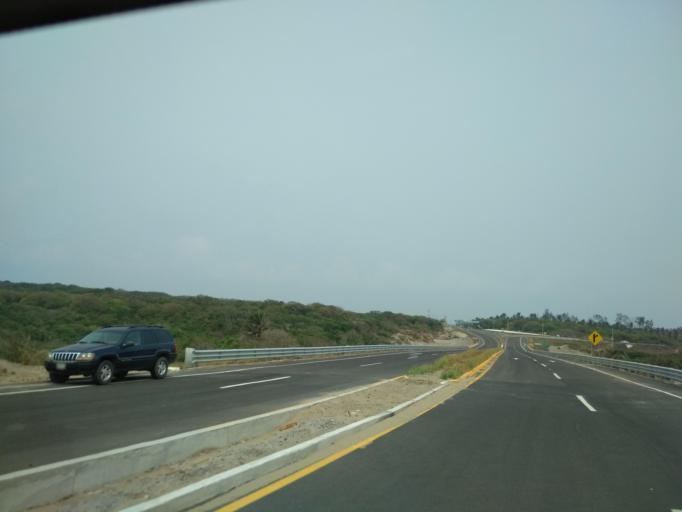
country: MX
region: Veracruz
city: Anton Lizardo
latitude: 19.0501
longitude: -96.0041
